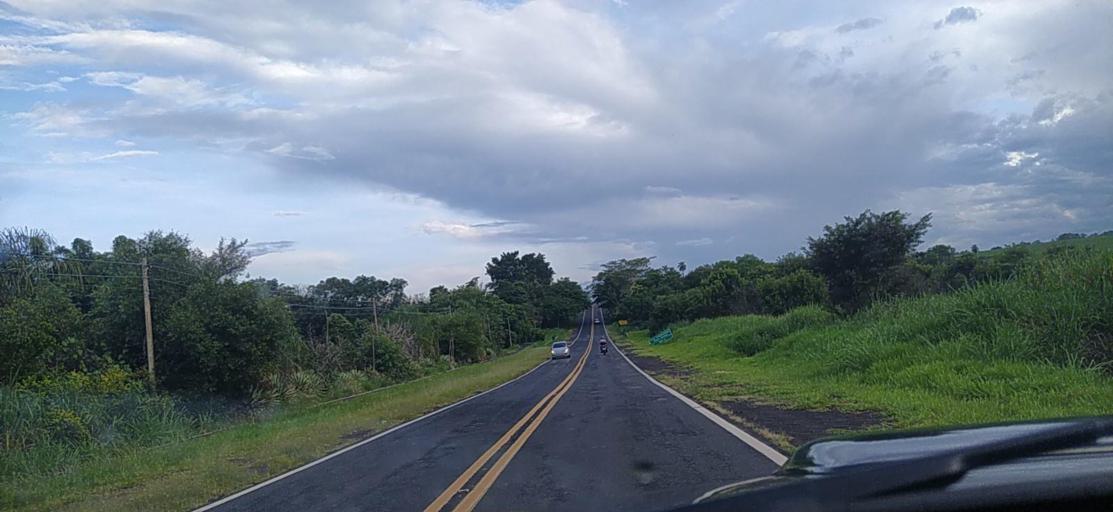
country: BR
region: Sao Paulo
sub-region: Catanduva
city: Catanduva
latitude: -21.1591
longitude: -48.9481
